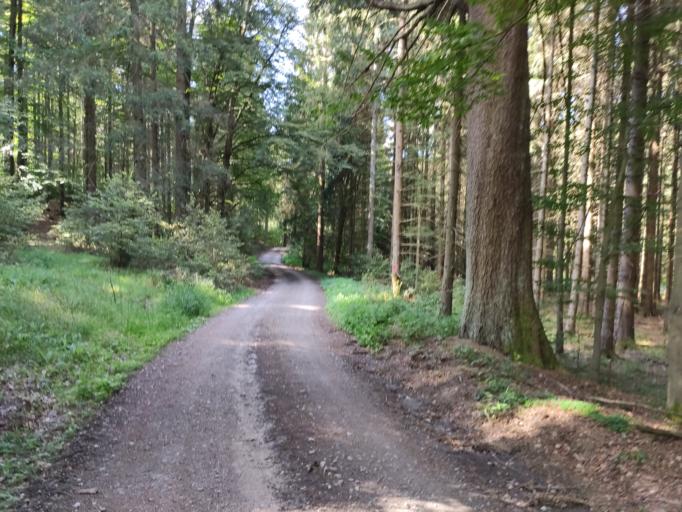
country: DE
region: Bavaria
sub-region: Upper Franconia
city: Nordhalben
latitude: 50.4131
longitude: 11.5388
